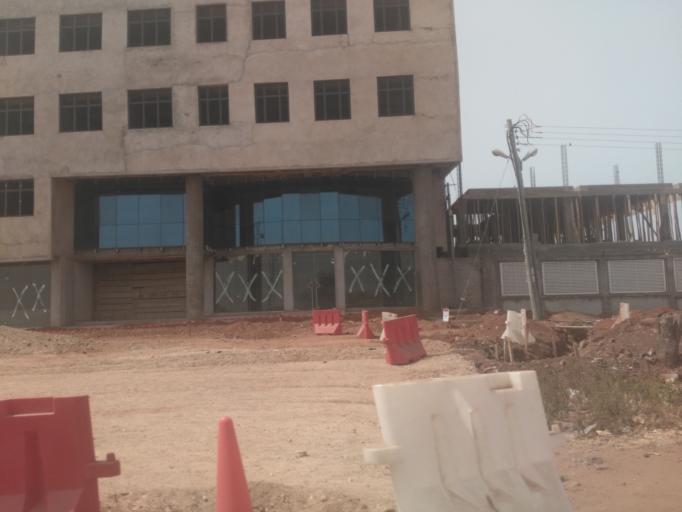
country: GH
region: Greater Accra
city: Tema
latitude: 5.6943
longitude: -0.0135
